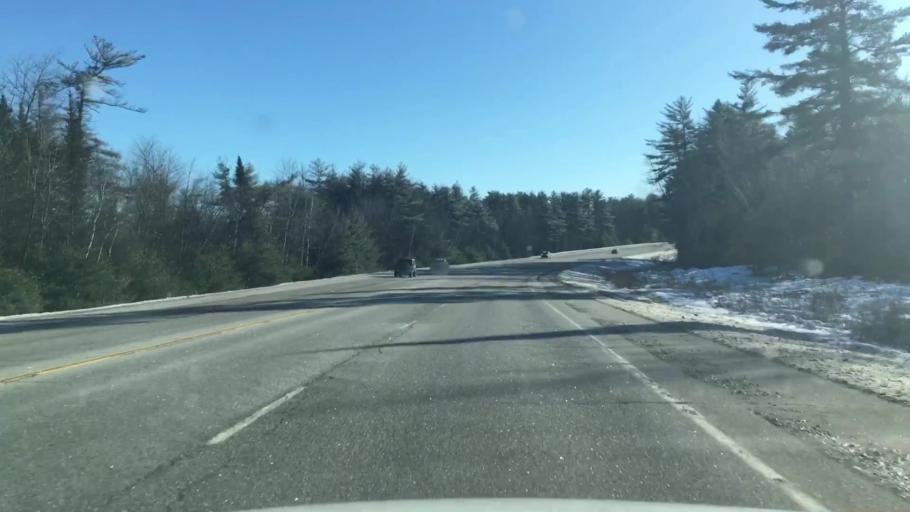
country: US
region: Maine
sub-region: Androscoggin County
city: Turner
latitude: 44.1803
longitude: -70.2327
